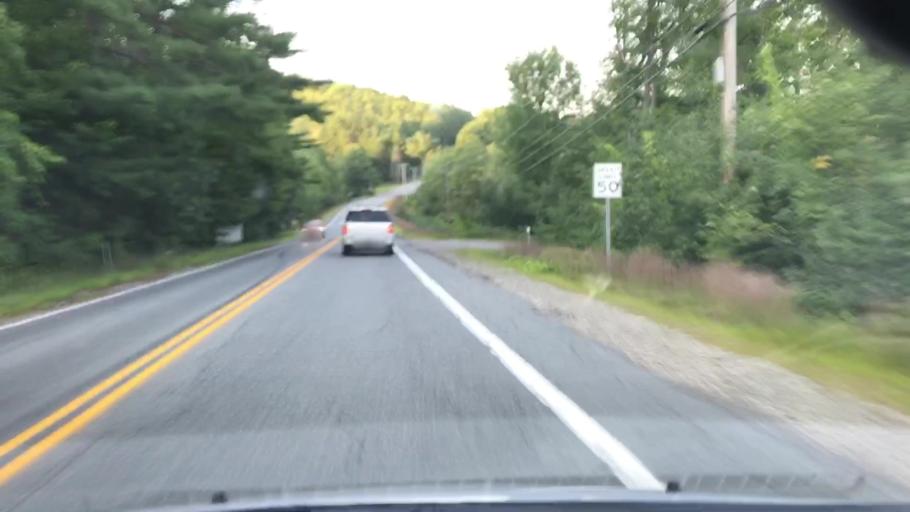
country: US
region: New Hampshire
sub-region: Grafton County
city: Rumney
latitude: 43.8783
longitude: -71.9113
